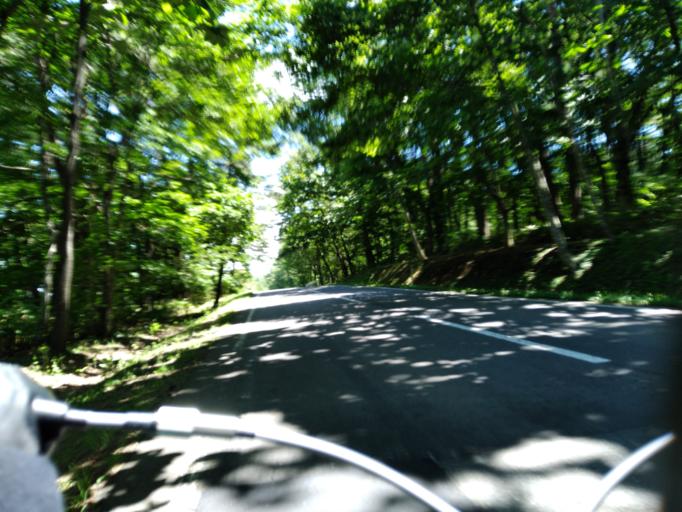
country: JP
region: Iwate
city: Shizukuishi
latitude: 39.7562
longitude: 141.0113
